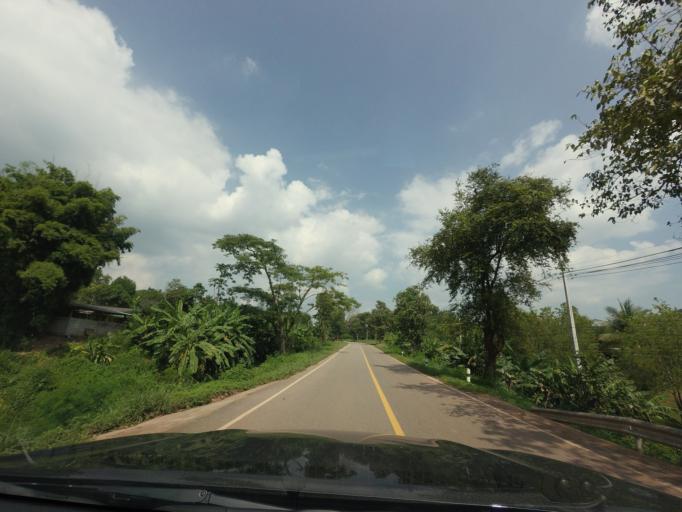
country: TH
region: Uttaradit
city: Ban Khok
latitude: 18.0285
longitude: 101.0791
